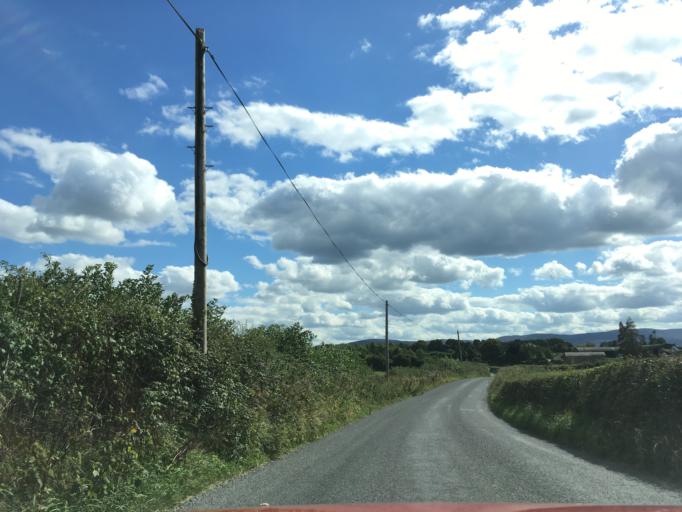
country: IE
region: Munster
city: Cashel
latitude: 52.4779
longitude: -7.9793
